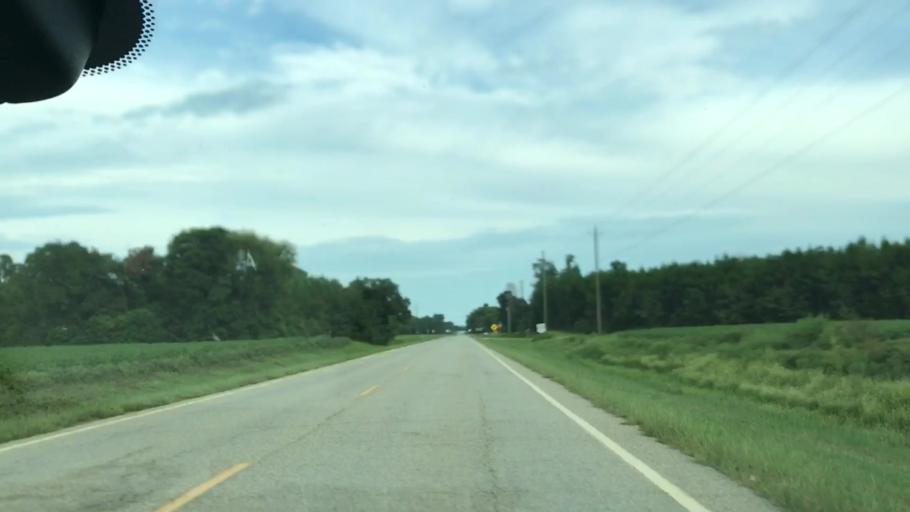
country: US
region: Georgia
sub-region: Quitman County
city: Georgetown
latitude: 31.7628
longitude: -85.0794
